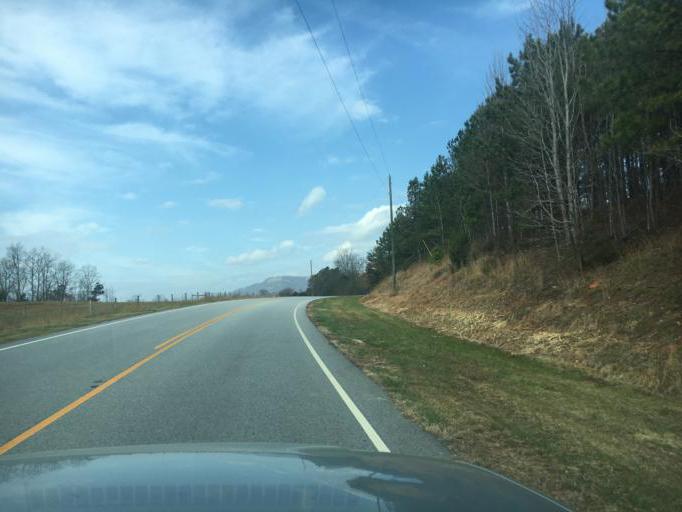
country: US
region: North Carolina
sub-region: Polk County
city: Tryon
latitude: 35.1250
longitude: -82.2632
